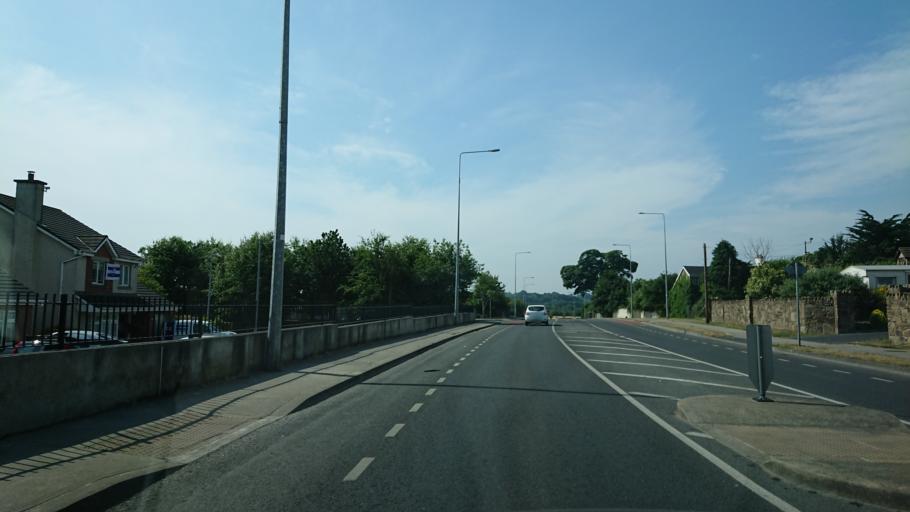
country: IE
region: Munster
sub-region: Waterford
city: Waterford
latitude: 52.2360
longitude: -7.1142
